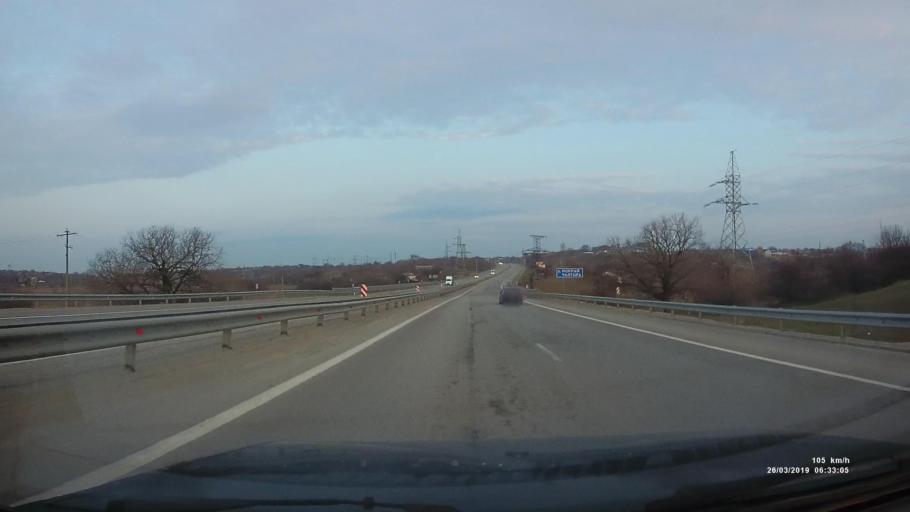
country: RU
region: Rostov
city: Chaltyr
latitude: 47.2715
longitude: 39.4962
